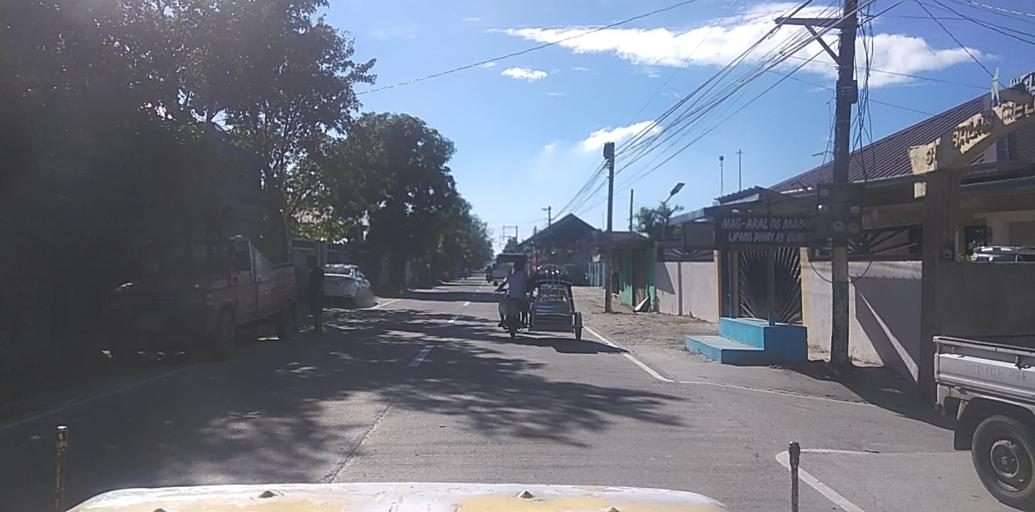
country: PH
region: Central Luzon
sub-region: Province of Pampanga
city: San Patricio
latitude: 15.0862
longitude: 120.7148
